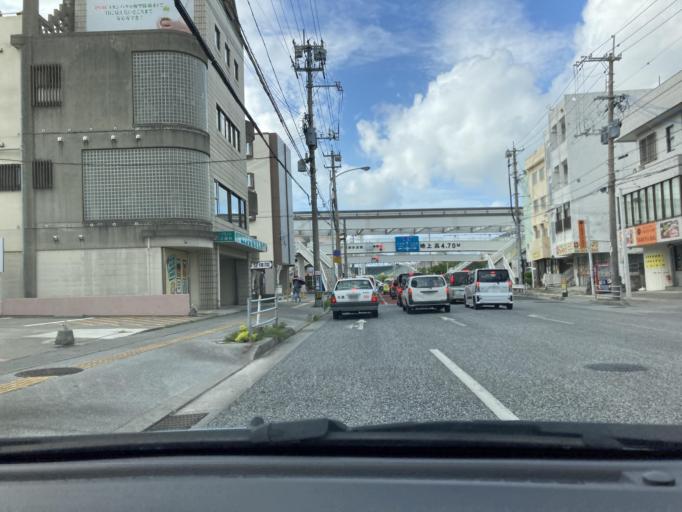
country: JP
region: Okinawa
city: Naha-shi
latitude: 26.1997
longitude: 127.6750
